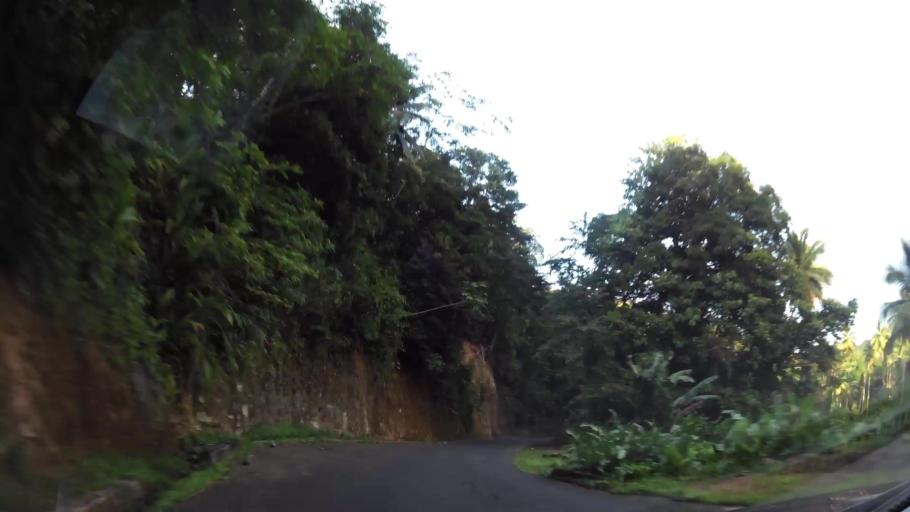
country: DM
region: Saint Andrew
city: Calibishie
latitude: 15.5889
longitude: -61.3993
